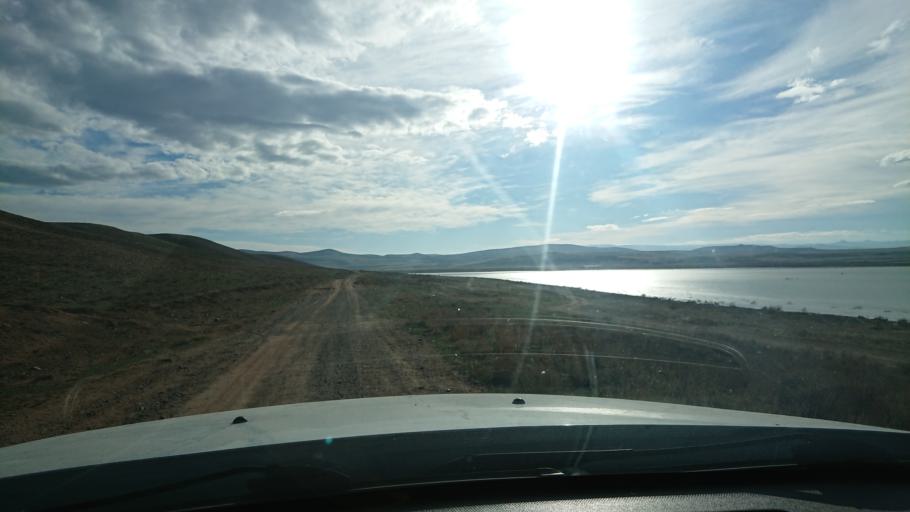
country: TR
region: Aksaray
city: Sariyahsi
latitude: 39.0490
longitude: 33.9736
